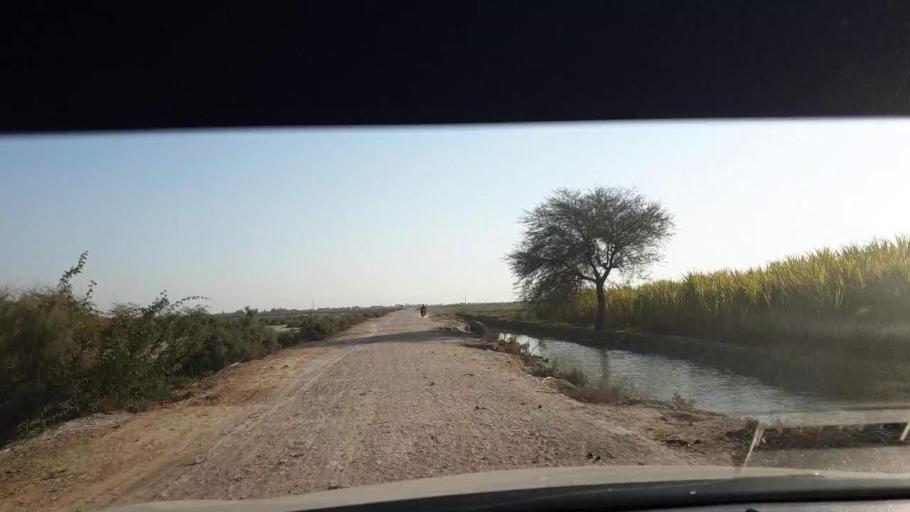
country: PK
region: Sindh
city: Berani
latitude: 25.7939
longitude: 68.9263
